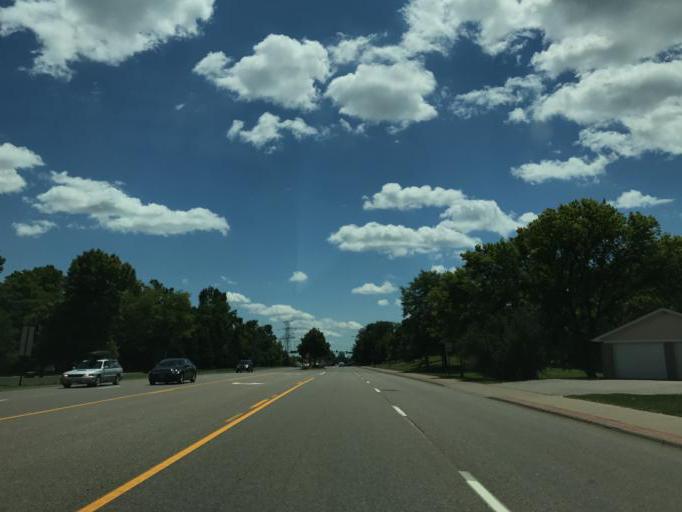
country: US
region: Minnesota
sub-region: Hennepin County
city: Maple Grove
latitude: 45.0711
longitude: -93.4535
